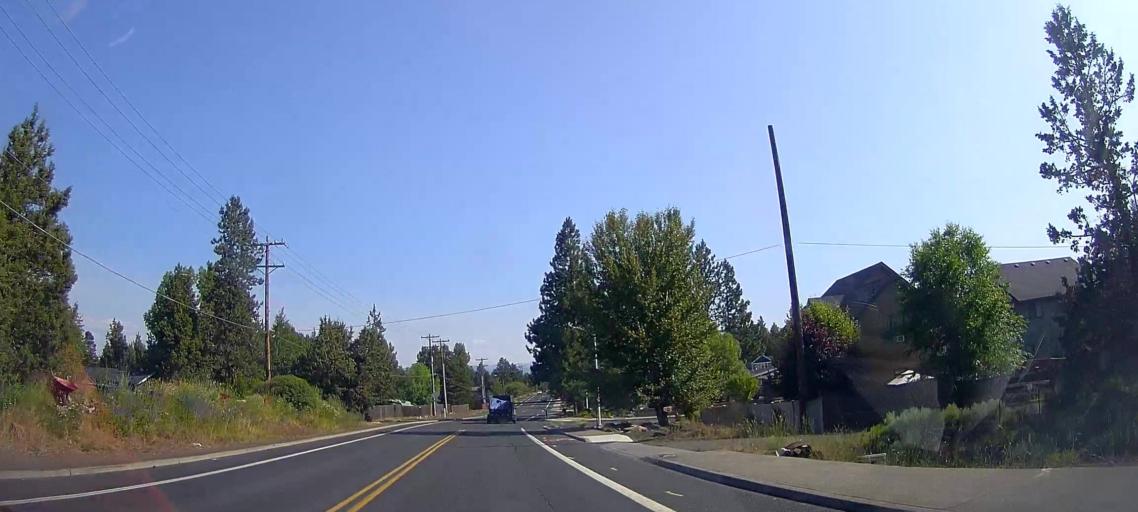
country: US
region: Oregon
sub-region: Deschutes County
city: Bend
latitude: 44.0353
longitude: -121.2838
